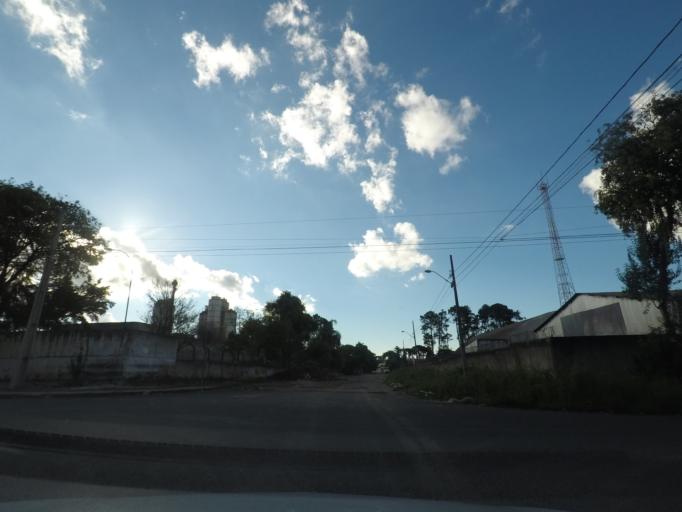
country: BR
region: Parana
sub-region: Curitiba
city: Curitiba
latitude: -25.4824
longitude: -49.2608
